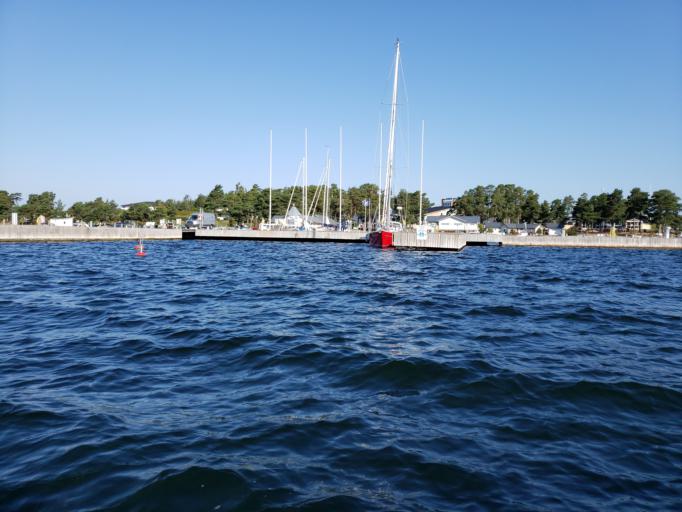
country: FI
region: Varsinais-Suomi
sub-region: Aboland-Turunmaa
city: Dragsfjaerd
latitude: 59.9198
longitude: 22.4106
